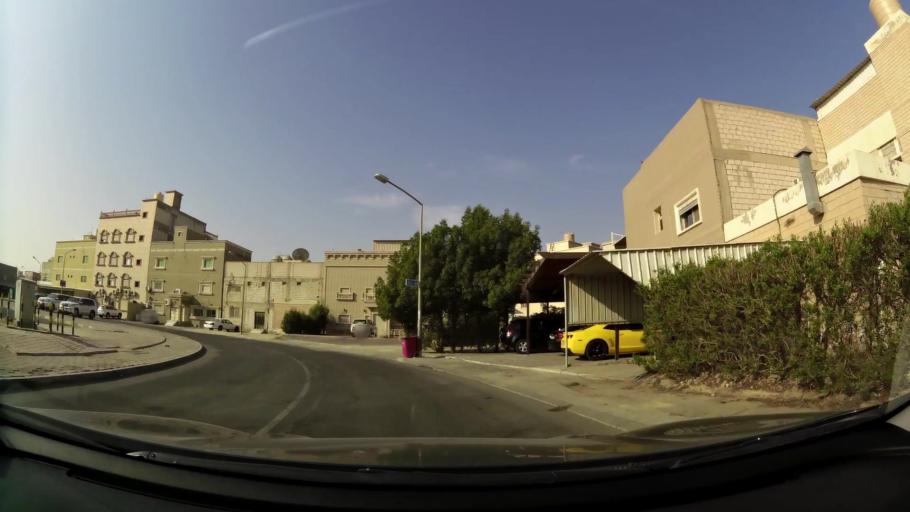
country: KW
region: Al Ahmadi
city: Ar Riqqah
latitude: 29.1594
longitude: 48.0661
